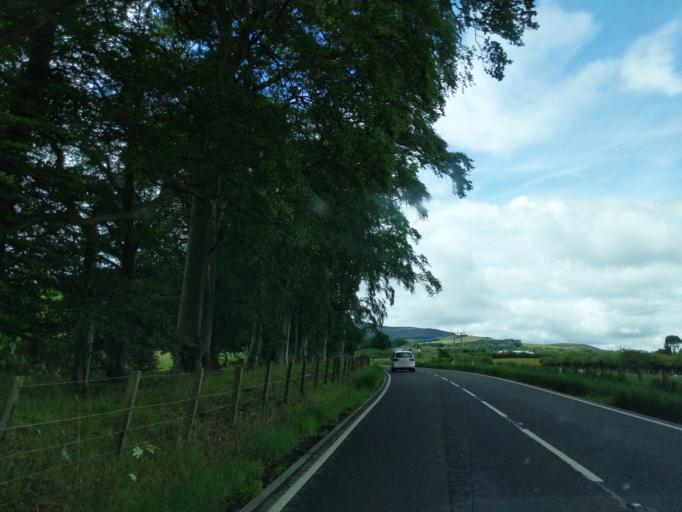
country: GB
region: Scotland
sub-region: South Lanarkshire
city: Biggar
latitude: 55.6051
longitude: -3.5885
